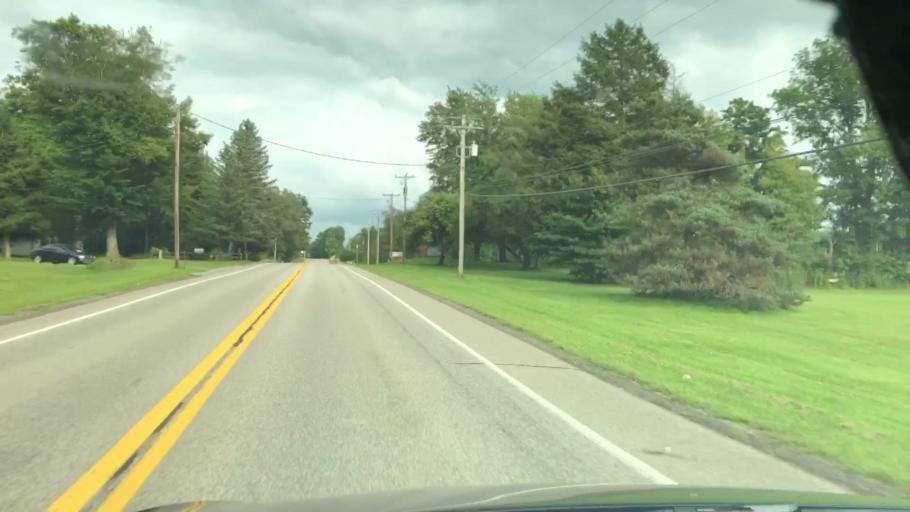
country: US
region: Pennsylvania
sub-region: Erie County
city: Northwest Harborcreek
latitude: 42.0571
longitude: -79.9077
